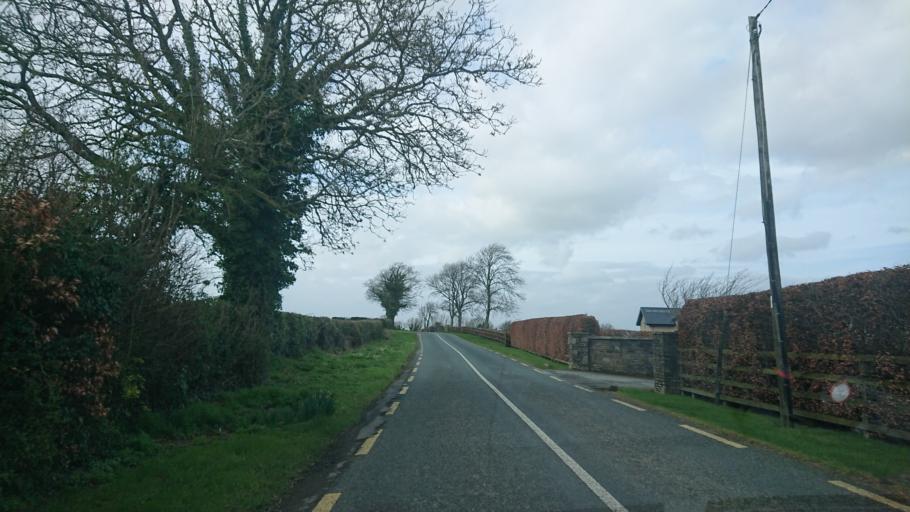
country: IE
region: Leinster
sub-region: Kildare
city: Naas
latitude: 53.1918
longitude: -6.6471
